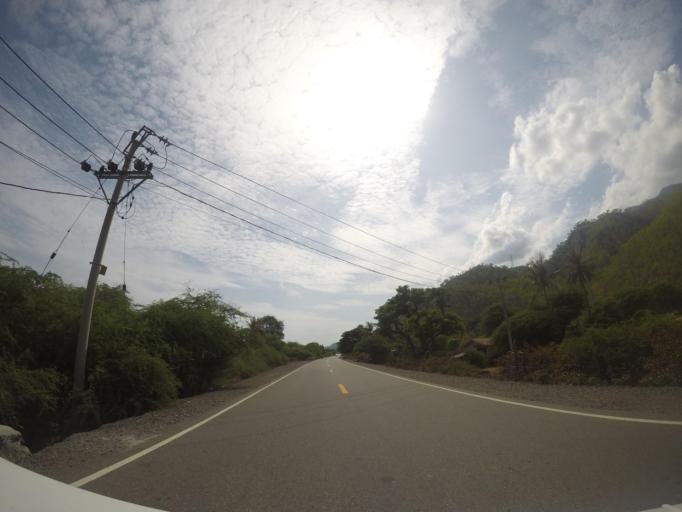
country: ID
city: Metinaro
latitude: -8.4766
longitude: 125.8597
